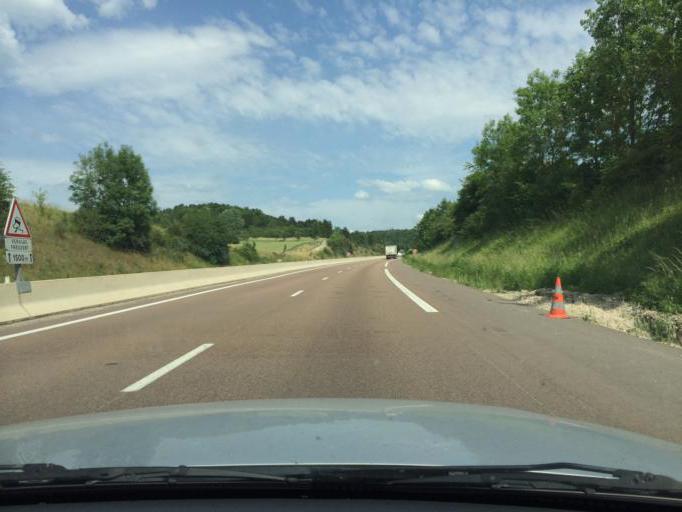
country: FR
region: Lorraine
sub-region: Departement de la Meuse
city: Ligny-en-Barrois
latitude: 48.6942
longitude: 5.3241
